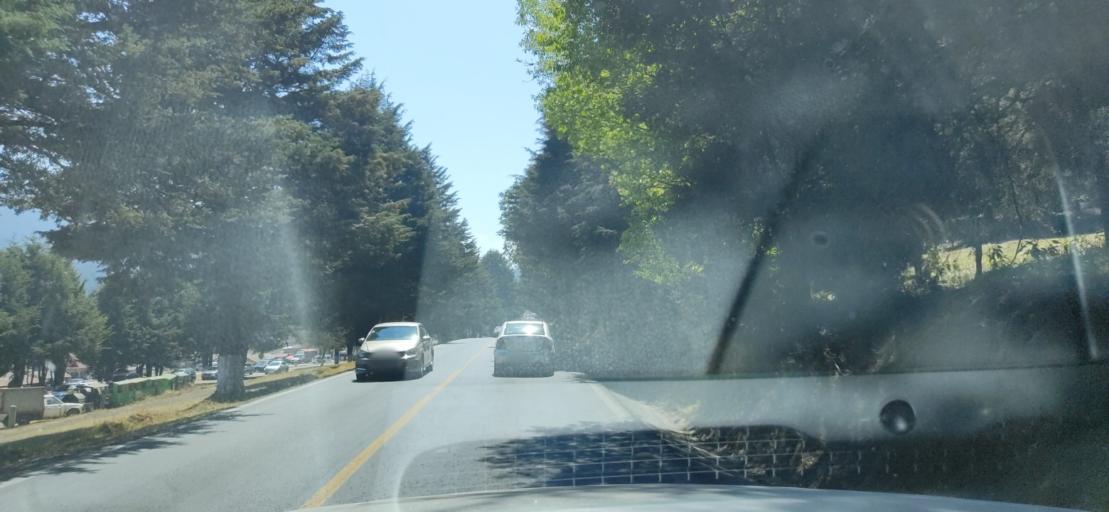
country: MX
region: Mexico
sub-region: Ocoyoacac
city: San Jeronimo Acazulco
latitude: 19.2885
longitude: -99.3740
